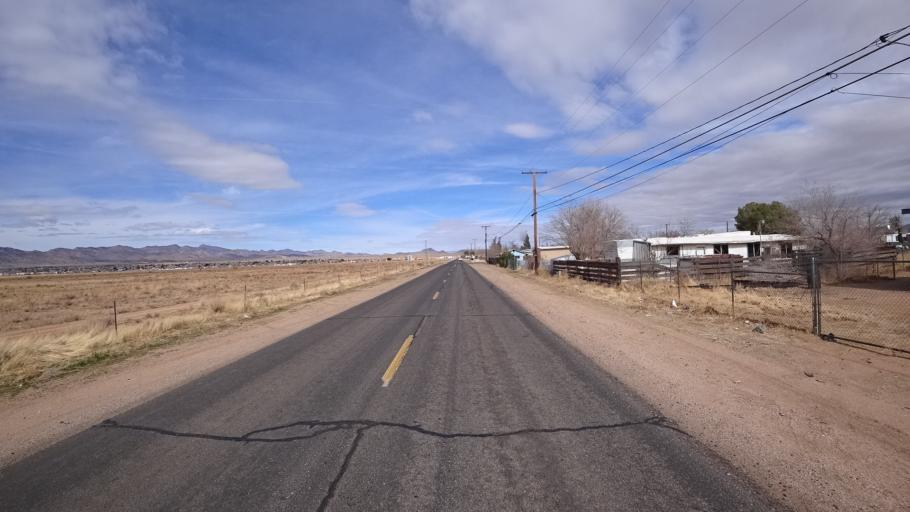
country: US
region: Arizona
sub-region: Mohave County
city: New Kingman-Butler
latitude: 35.2455
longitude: -113.9938
